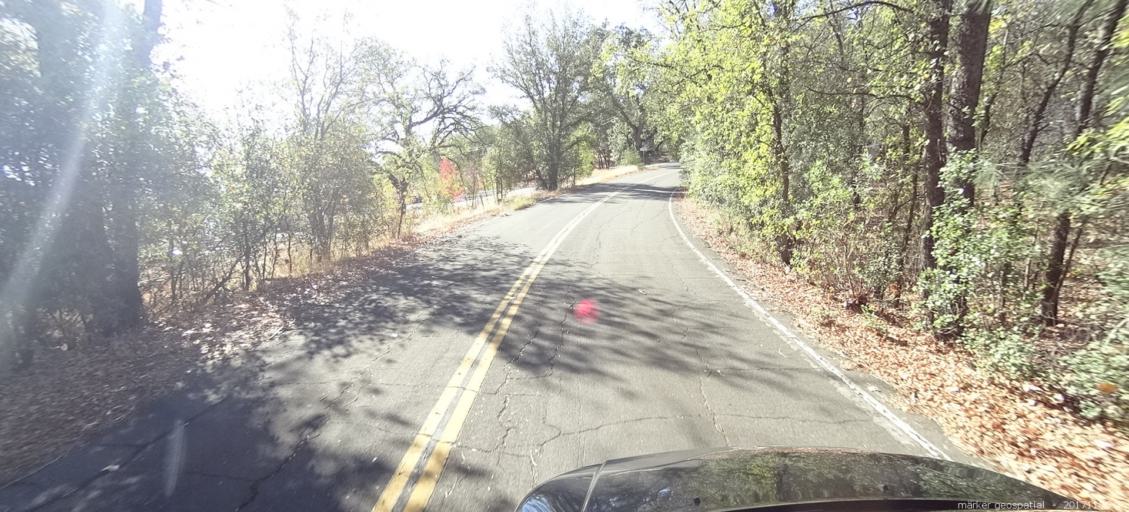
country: US
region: California
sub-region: Shasta County
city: Palo Cedro
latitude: 40.5934
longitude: -122.2348
